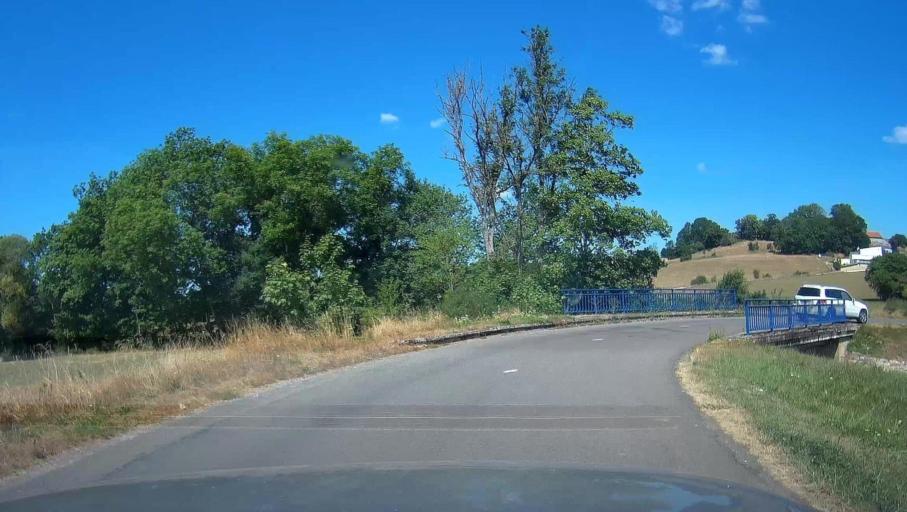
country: FR
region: Champagne-Ardenne
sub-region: Departement de la Haute-Marne
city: Langres
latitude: 47.8655
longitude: 5.3729
